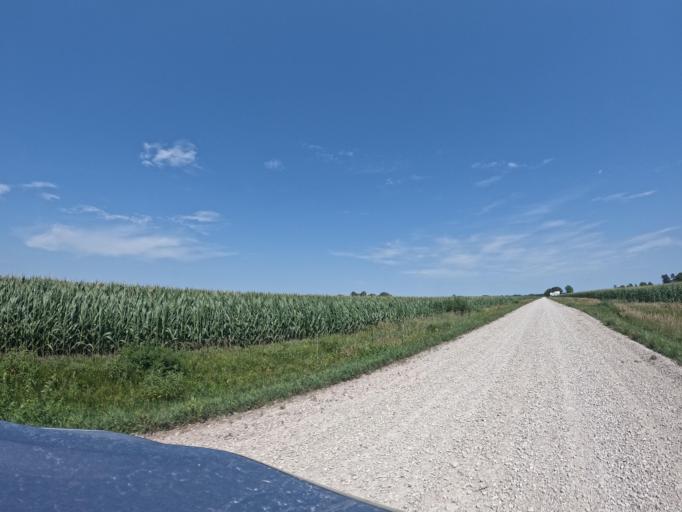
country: US
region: Iowa
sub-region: Henry County
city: Mount Pleasant
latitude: 40.9013
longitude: -91.6377
